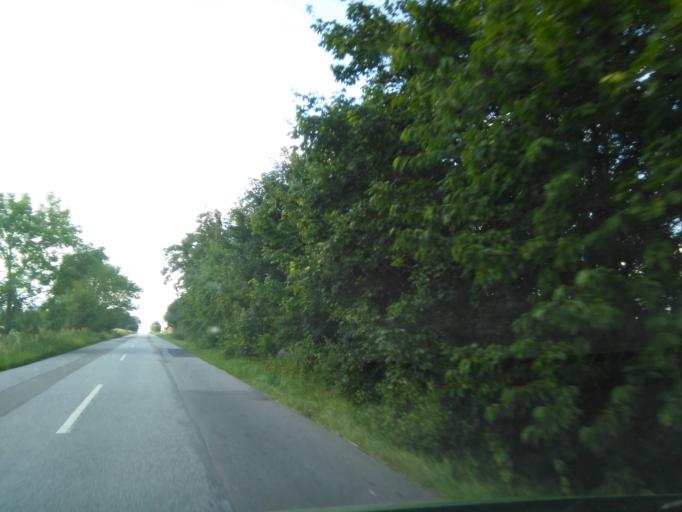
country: DK
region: Central Jutland
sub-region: Arhus Kommune
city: Solbjerg
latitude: 56.0614
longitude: 10.0919
